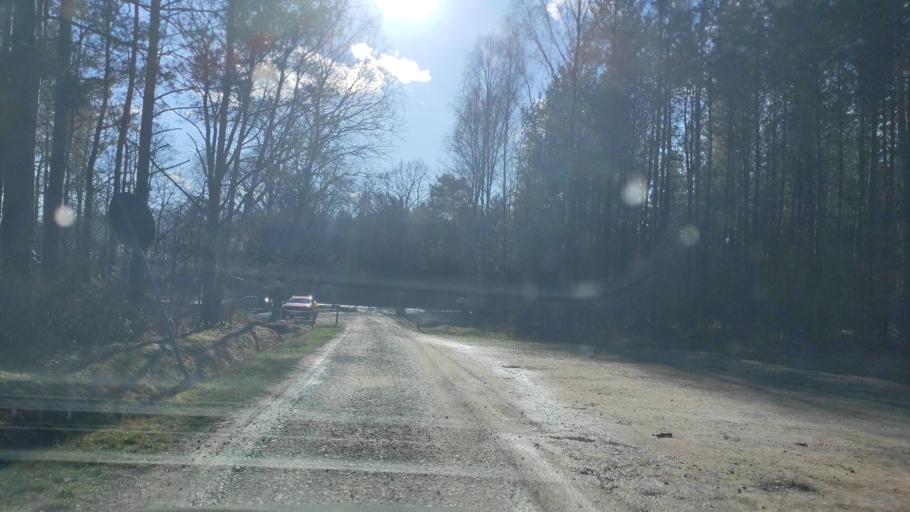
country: PL
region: Masovian Voivodeship
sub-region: Powiat radomski
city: Jastrzebia
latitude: 51.4657
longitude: 21.2312
